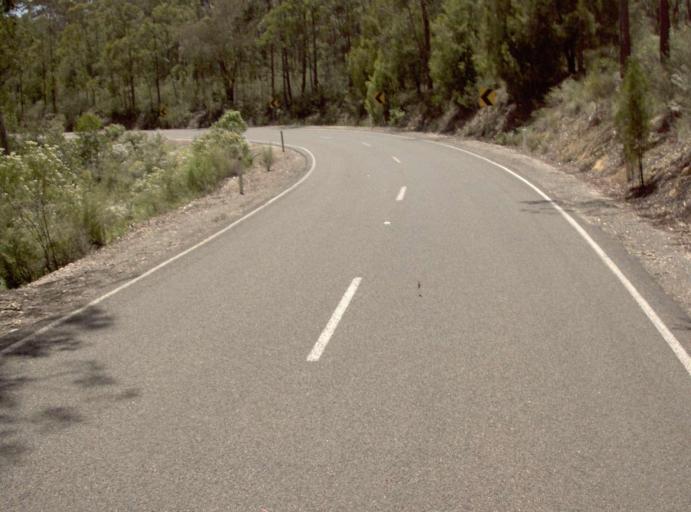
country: AU
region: Victoria
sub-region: East Gippsland
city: Lakes Entrance
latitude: -37.5848
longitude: 147.8946
